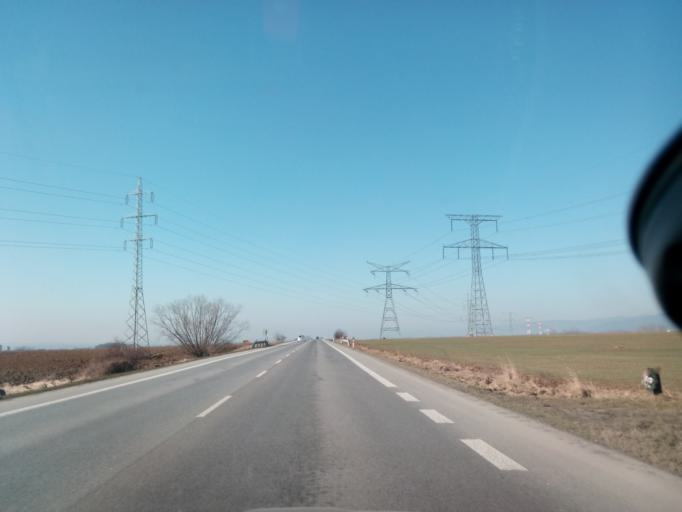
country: SK
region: Kosicky
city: Moldava nad Bodvou
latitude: 48.6050
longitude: 21.1011
